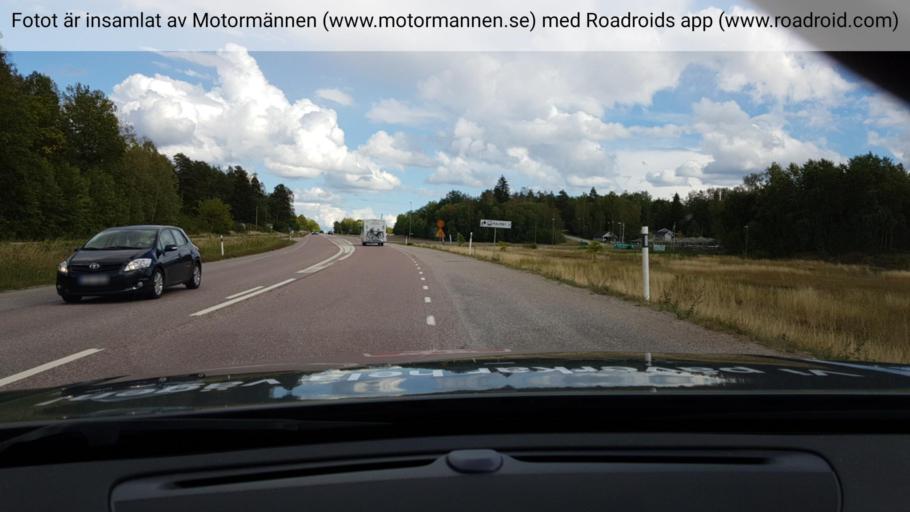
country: SE
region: Soedermanland
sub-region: Strangnas Kommun
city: Strangnas
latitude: 59.3408
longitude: 17.0399
